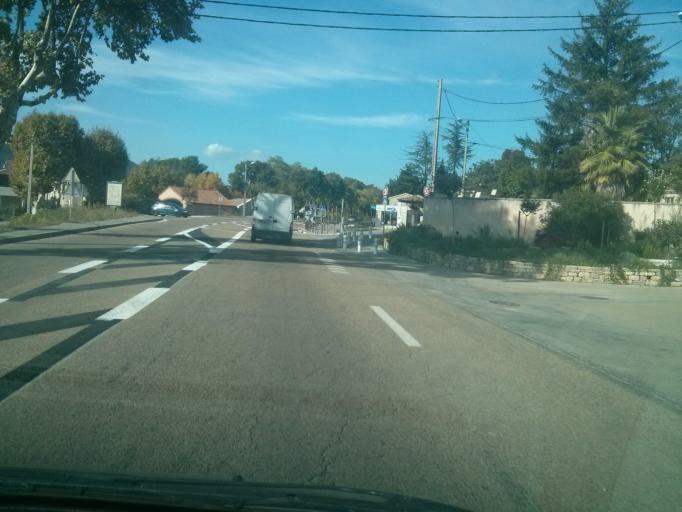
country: FR
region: Languedoc-Roussillon
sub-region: Departement du Gard
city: Quissac
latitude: 43.9072
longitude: 4.0043
